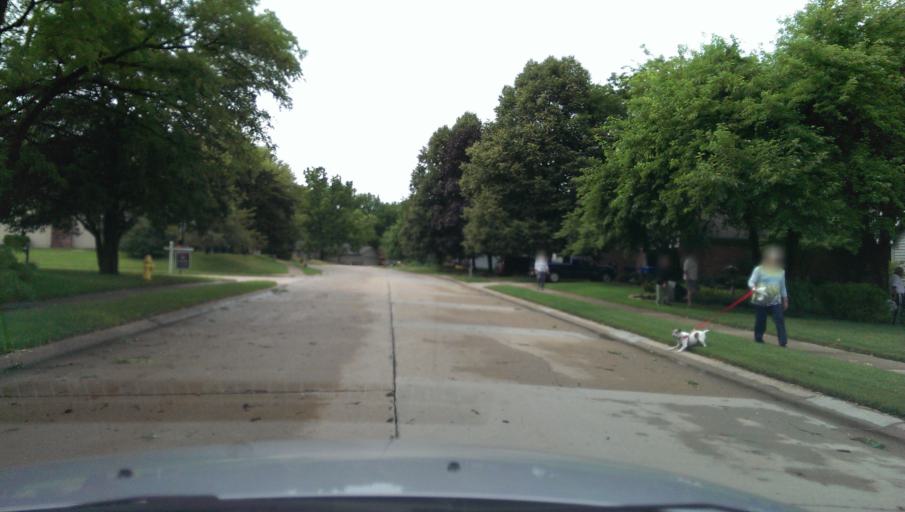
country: US
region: Indiana
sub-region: Hamilton County
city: Carmel
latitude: 39.9950
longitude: -86.1347
